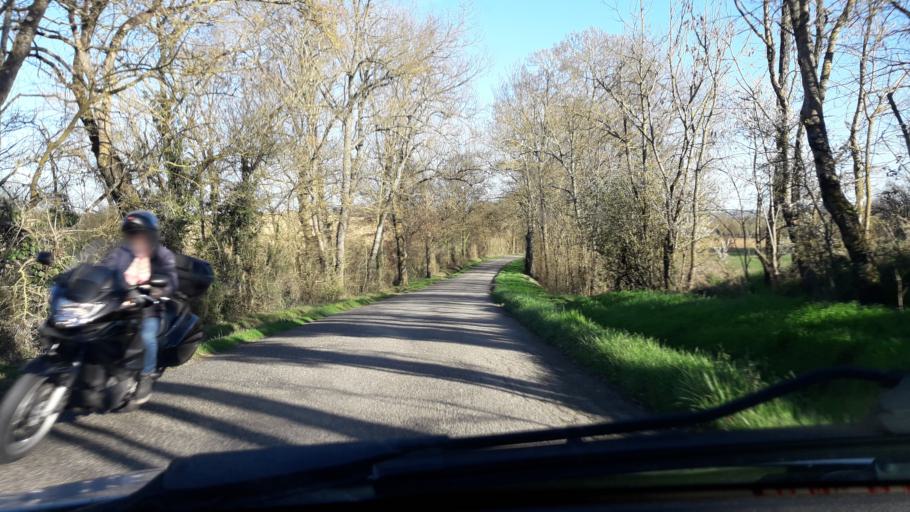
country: FR
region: Midi-Pyrenees
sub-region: Departement du Gers
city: Gimont
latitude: 43.6232
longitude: 1.0116
